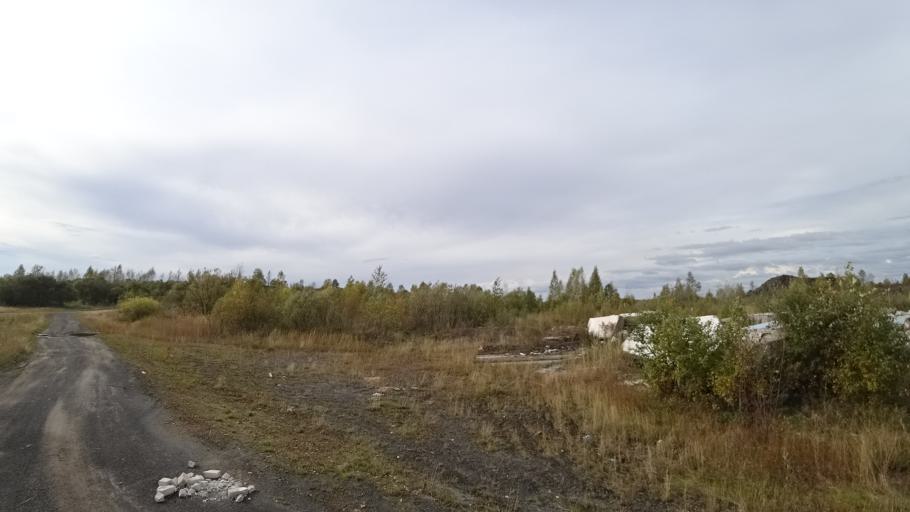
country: RU
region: Amur
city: Arkhara
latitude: 49.3119
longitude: 130.1796
